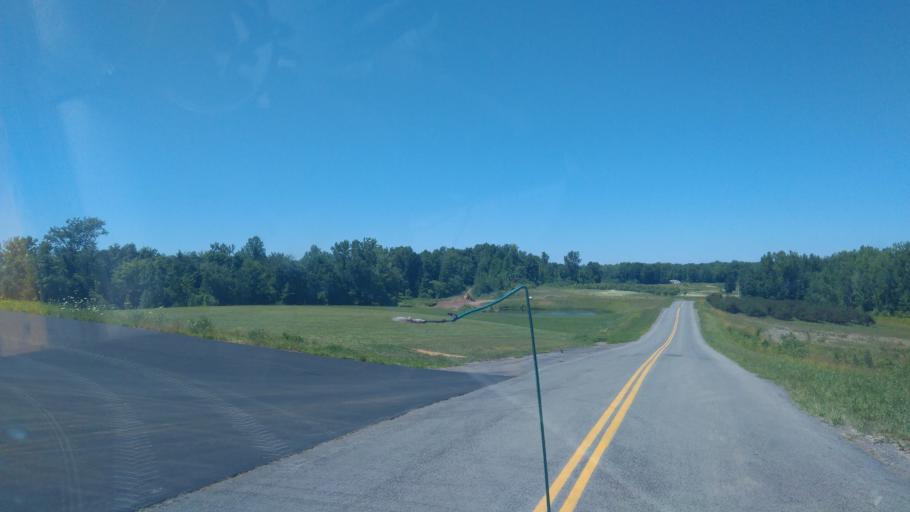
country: US
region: New York
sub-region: Wayne County
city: Lyons
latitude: 43.1579
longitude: -76.9795
